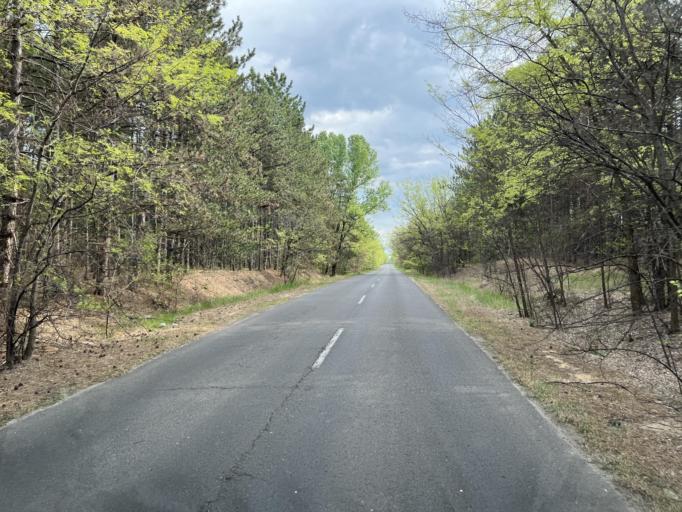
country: HU
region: Pest
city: Farmos
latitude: 47.3586
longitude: 19.7960
